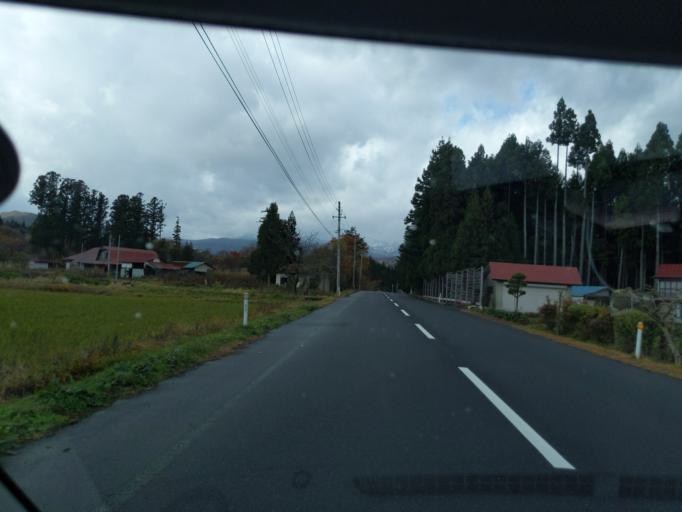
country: JP
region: Iwate
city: Mizusawa
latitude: 39.1114
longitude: 140.9623
